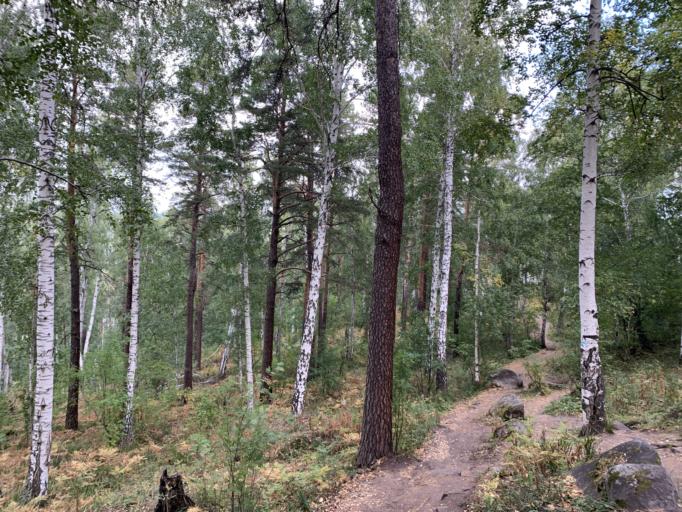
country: RU
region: Chelyabinsk
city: Vishnevogorsk
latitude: 55.9902
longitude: 60.4907
